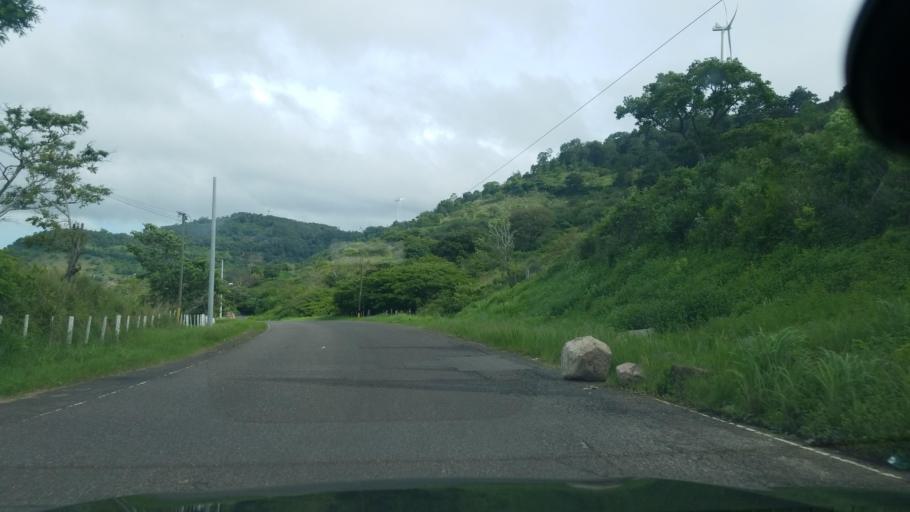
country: HN
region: Choluteca
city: Corpus
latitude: 13.3682
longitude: -86.9332
